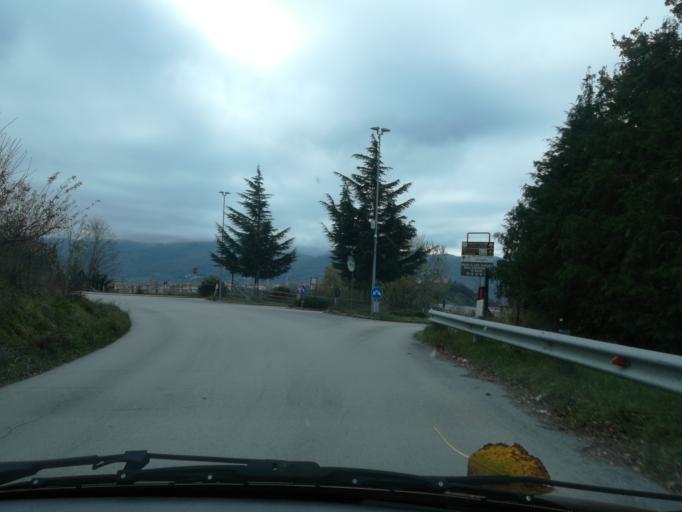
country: IT
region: Molise
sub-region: Provincia di Isernia
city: Agnone
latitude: 41.8176
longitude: 14.3724
